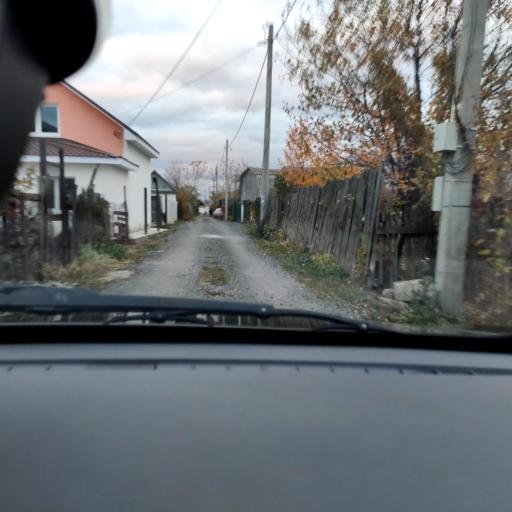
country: RU
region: Samara
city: Tol'yatti
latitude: 53.5398
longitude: 49.4289
